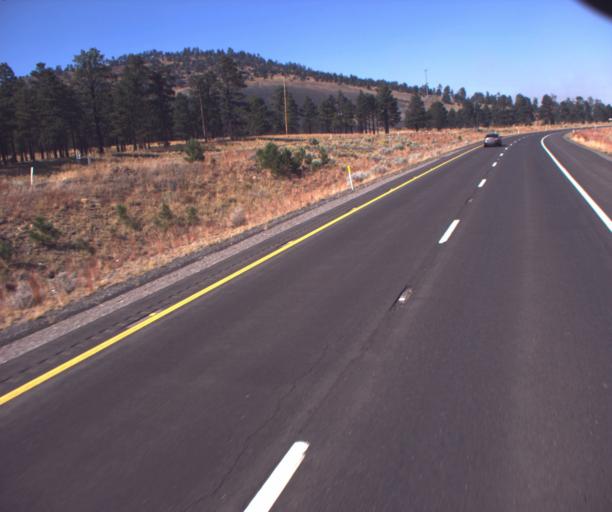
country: US
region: Arizona
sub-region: Coconino County
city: Flagstaff
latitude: 35.3793
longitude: -111.5796
